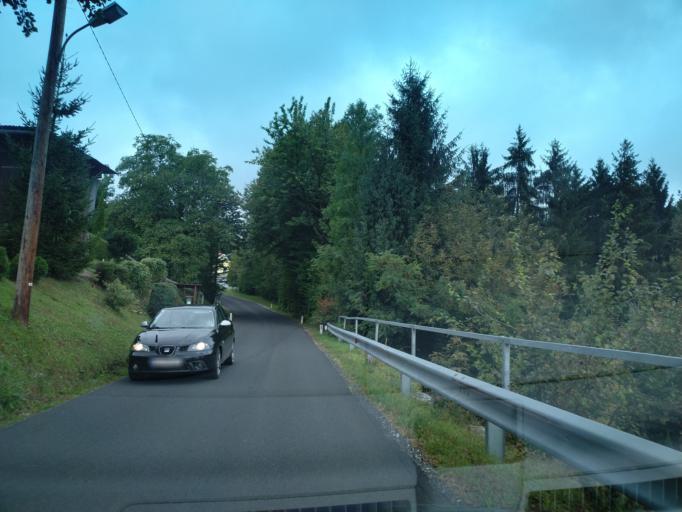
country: AT
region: Styria
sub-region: Politischer Bezirk Deutschlandsberg
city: Deutschlandsberg
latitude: 46.8238
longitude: 15.2034
